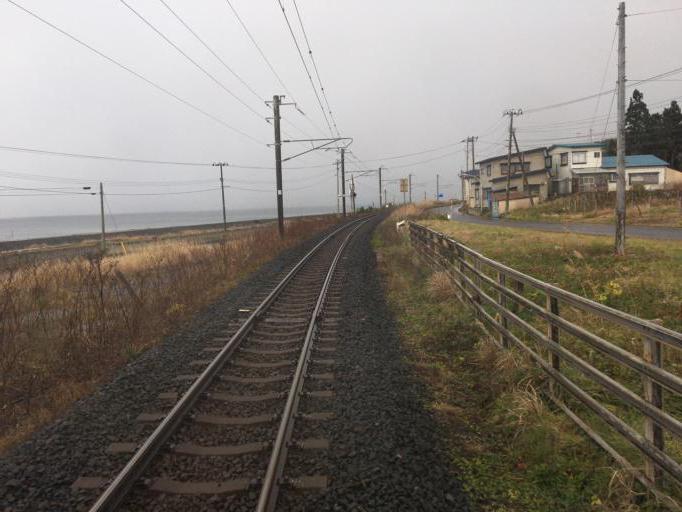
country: JP
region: Aomori
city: Aomori Shi
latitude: 41.0359
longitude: 140.6450
